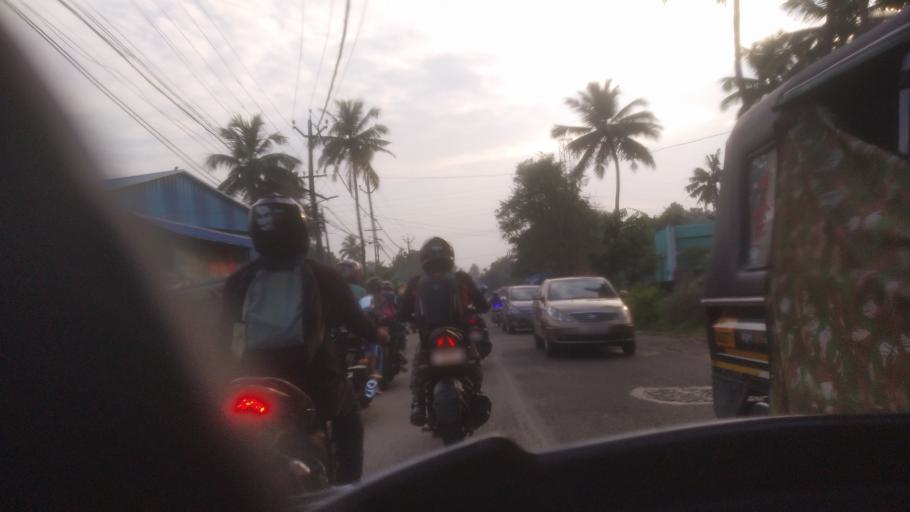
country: IN
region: Kerala
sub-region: Ernakulam
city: Perumpavur
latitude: 10.1161
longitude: 76.4576
